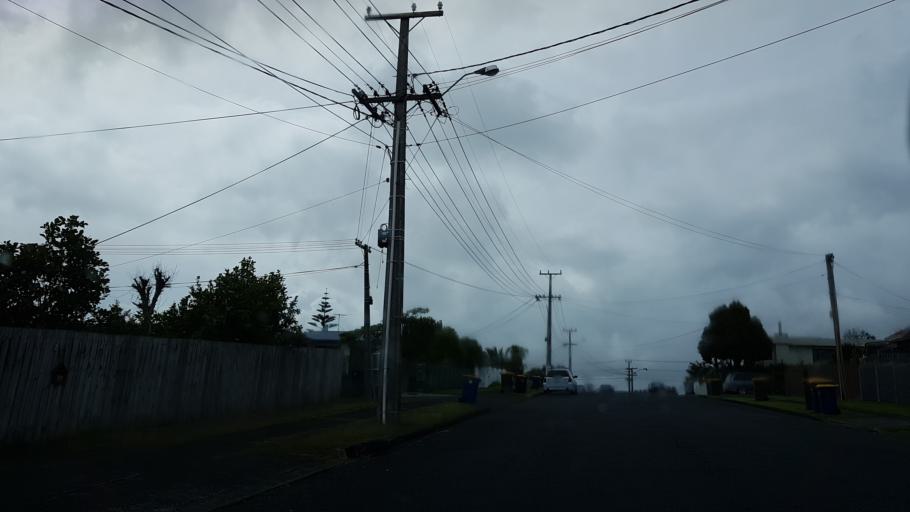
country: NZ
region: Auckland
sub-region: Auckland
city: North Shore
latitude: -36.7886
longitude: 174.7322
